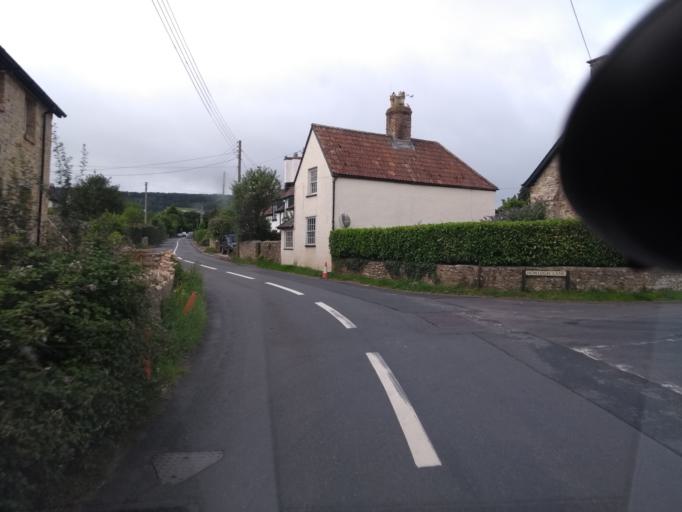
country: GB
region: England
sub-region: Somerset
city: Taunton
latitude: 50.9639
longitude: -3.1239
